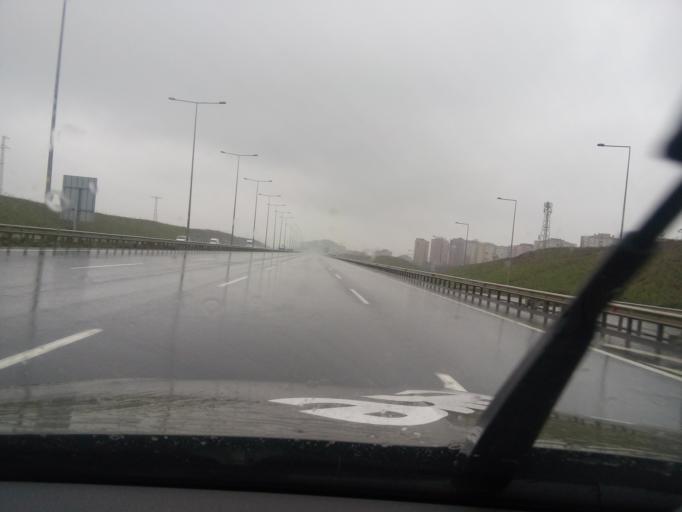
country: TR
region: Istanbul
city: Basaksehir
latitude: 41.1064
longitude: 28.8144
